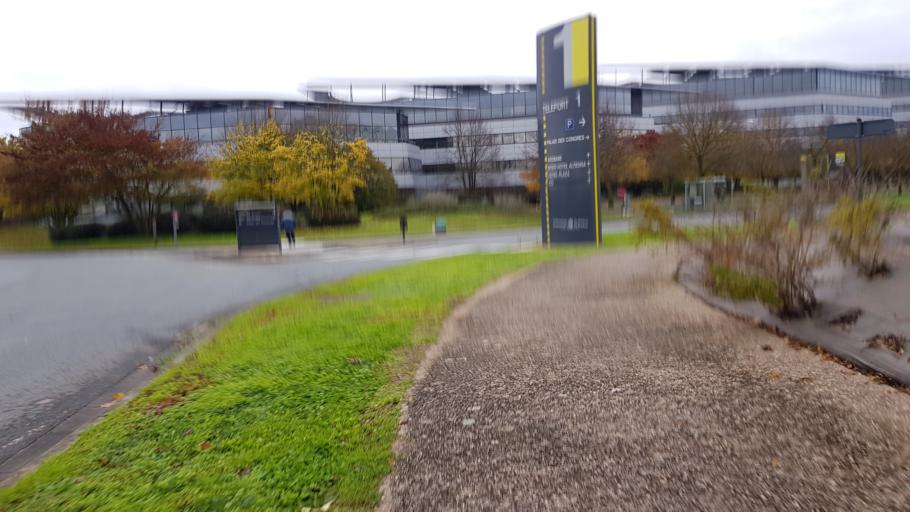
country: FR
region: Poitou-Charentes
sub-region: Departement de la Vienne
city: Chasseneuil-du-Poitou
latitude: 46.6610
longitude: 0.3653
